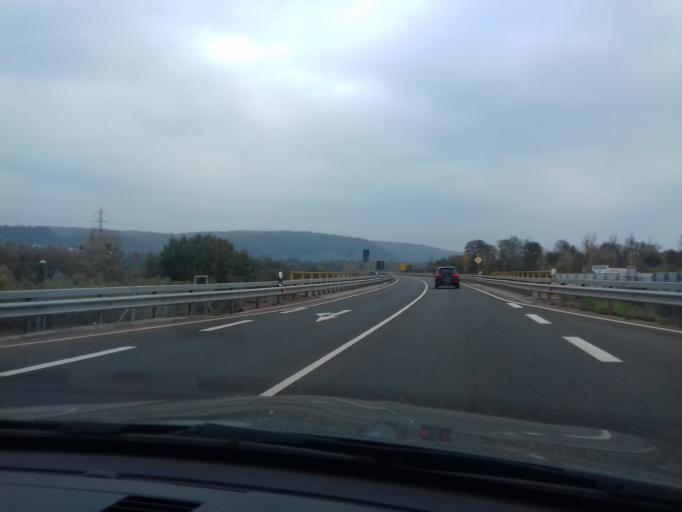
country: DE
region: Rheinland-Pfalz
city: Konz
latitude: 49.6955
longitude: 6.5570
